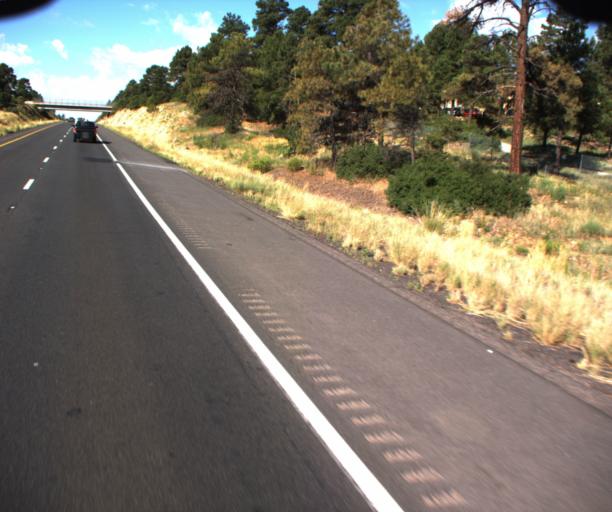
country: US
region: Arizona
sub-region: Coconino County
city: Flagstaff
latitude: 35.2039
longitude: -111.6061
